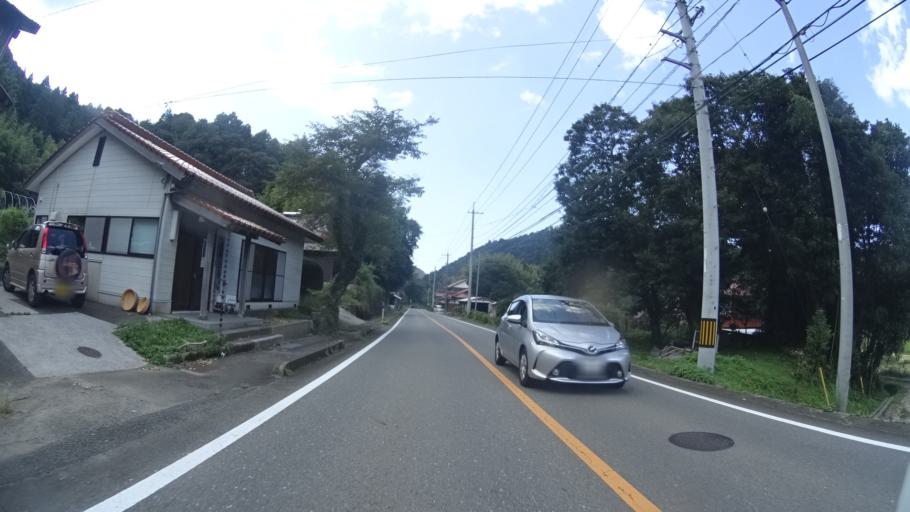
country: JP
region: Yamaguchi
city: Hagi
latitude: 34.4363
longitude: 131.4651
